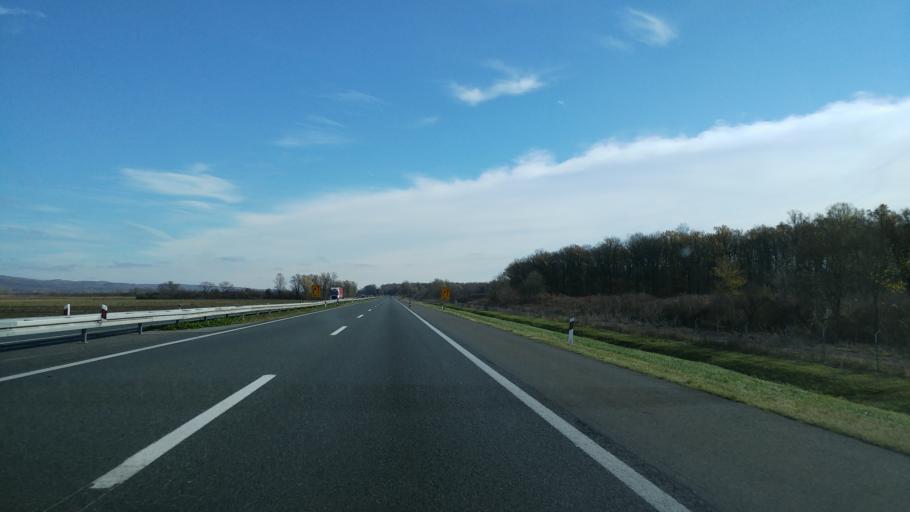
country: HR
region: Sisacko-Moslavacka
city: Novska
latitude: 45.2992
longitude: 17.0573
